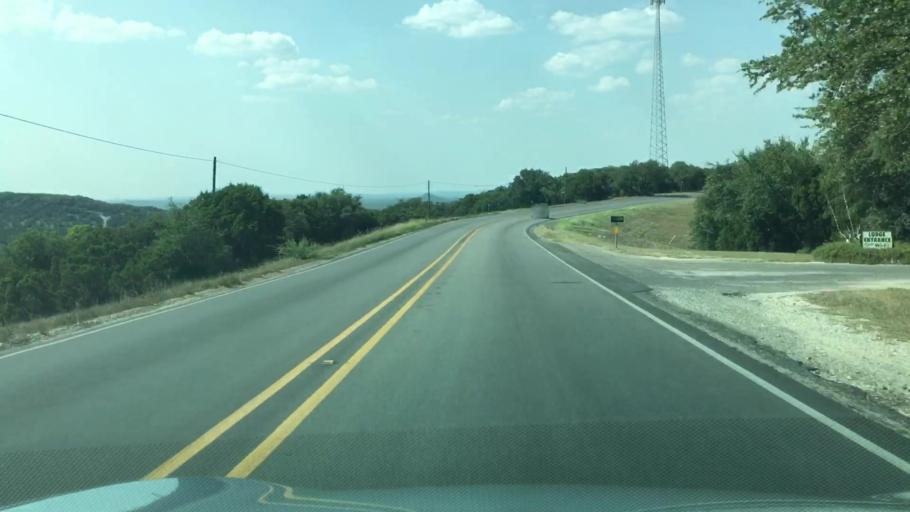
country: US
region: Texas
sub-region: Hays County
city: Wimberley
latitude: 29.9574
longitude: -98.0948
